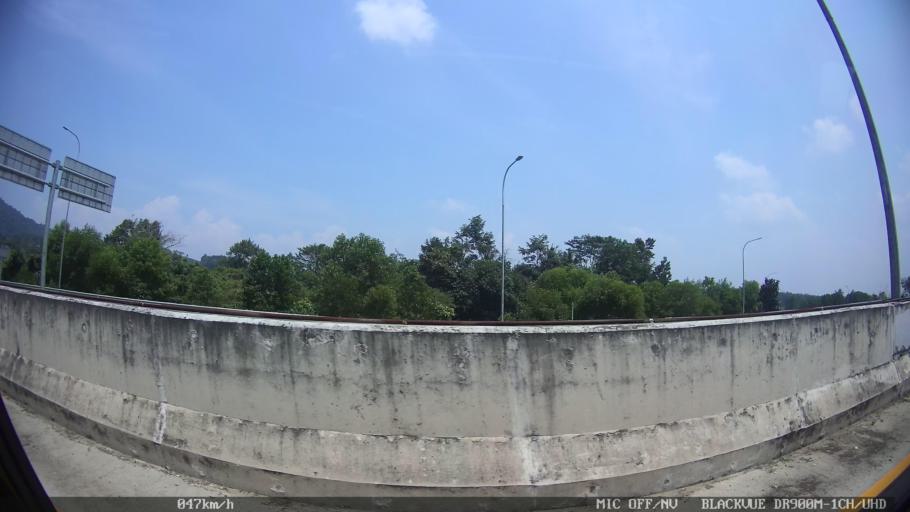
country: ID
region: Lampung
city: Panjang
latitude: -5.3966
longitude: 105.3490
